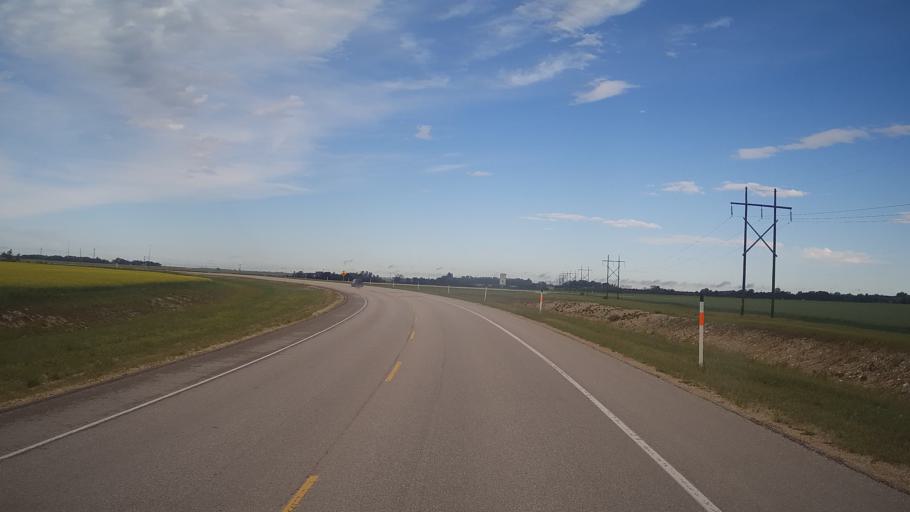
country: CA
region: Manitoba
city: Stonewall
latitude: 50.1228
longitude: -97.5223
